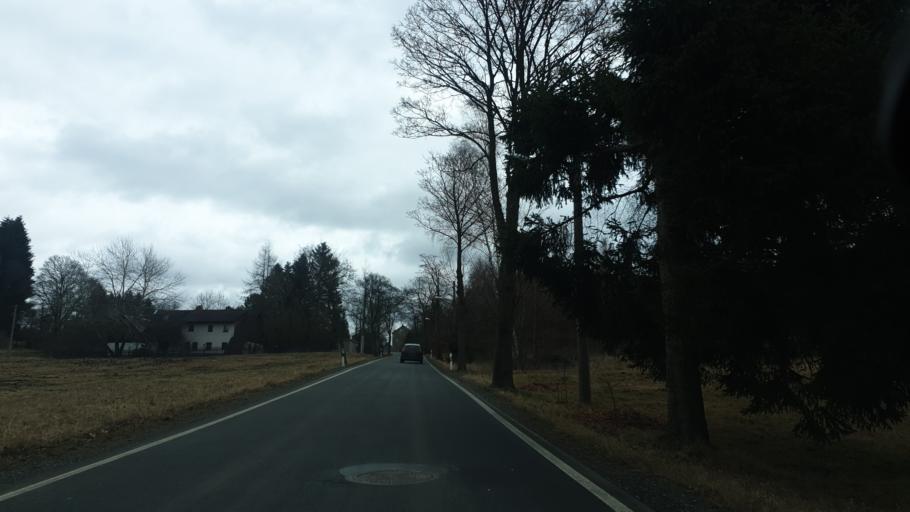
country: DE
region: Saxony
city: Bad Elster
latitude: 50.2756
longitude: 12.2620
